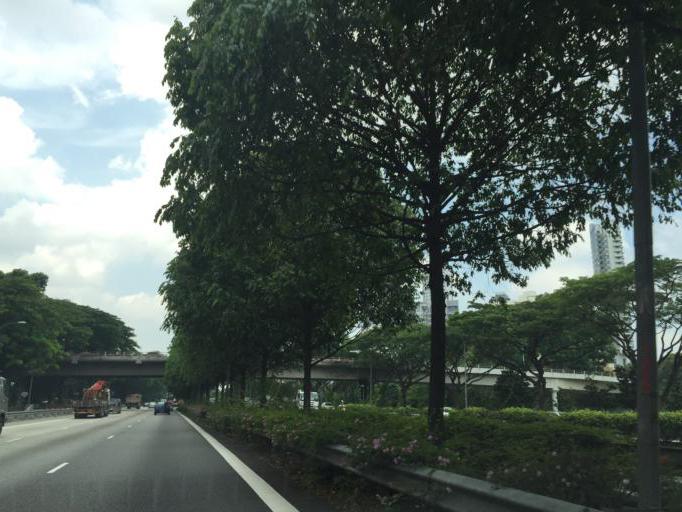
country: SG
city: Singapore
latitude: 1.3298
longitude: 103.8450
